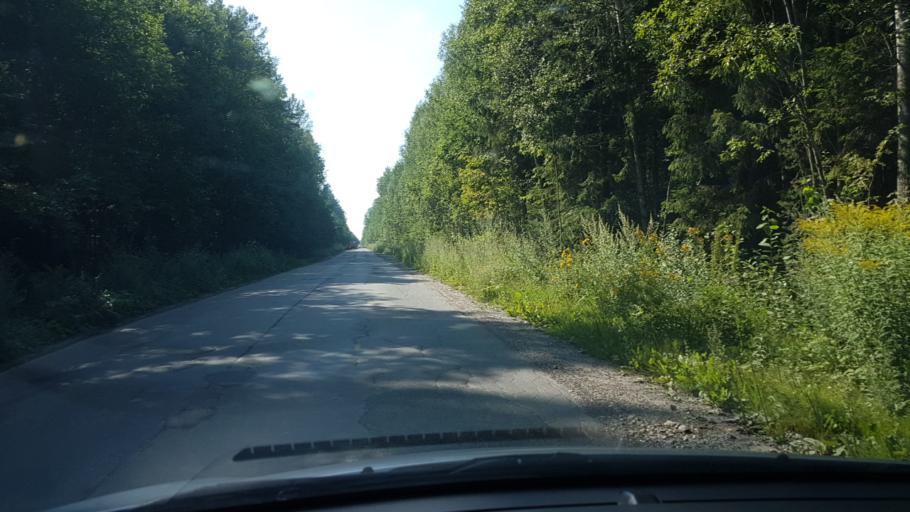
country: RU
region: Leningrad
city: Vyritsa
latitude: 59.4488
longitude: 30.3153
